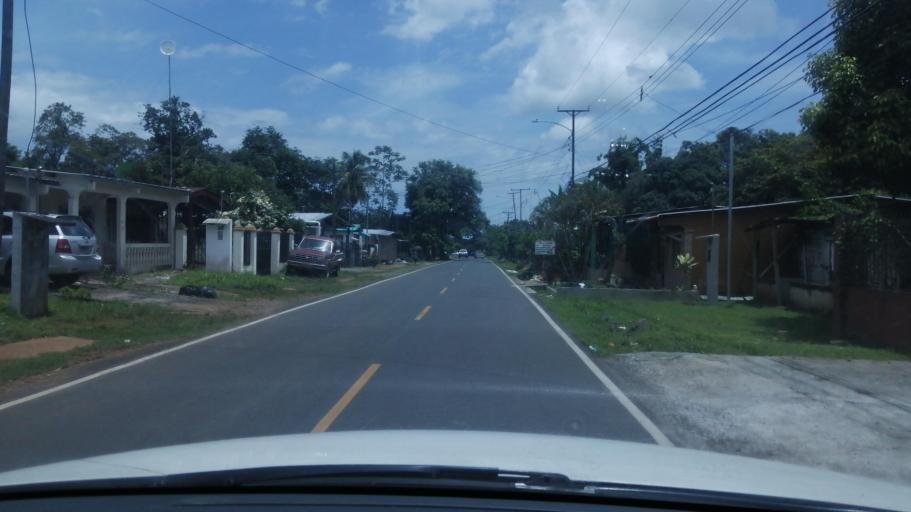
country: PA
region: Chiriqui
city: David
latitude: 8.4185
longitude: -82.4267
